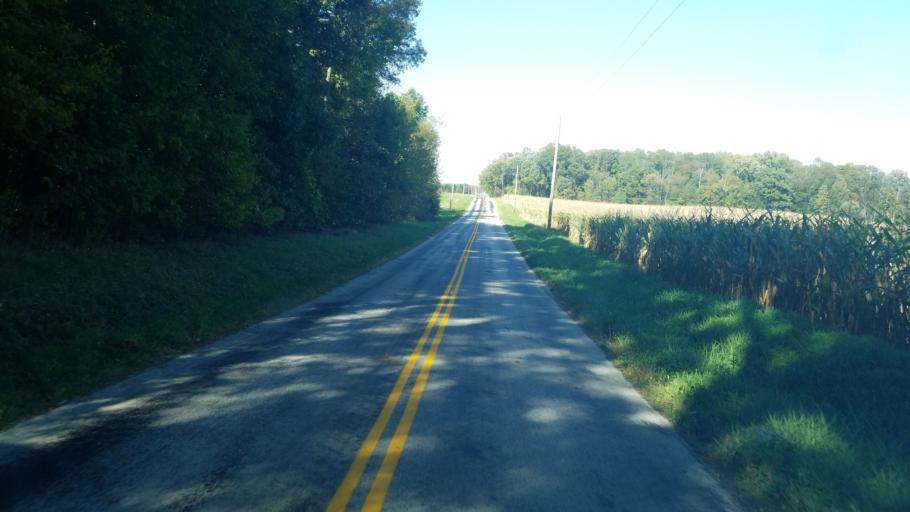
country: US
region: Ohio
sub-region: Huron County
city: New London
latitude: 41.0028
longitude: -82.3737
